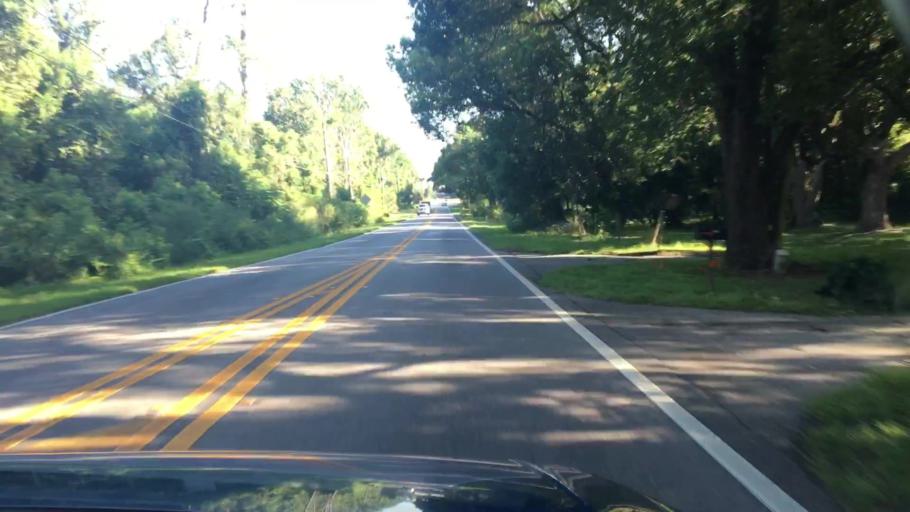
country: US
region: Florida
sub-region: Lake County
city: Eustis
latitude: 28.8599
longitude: -81.6529
